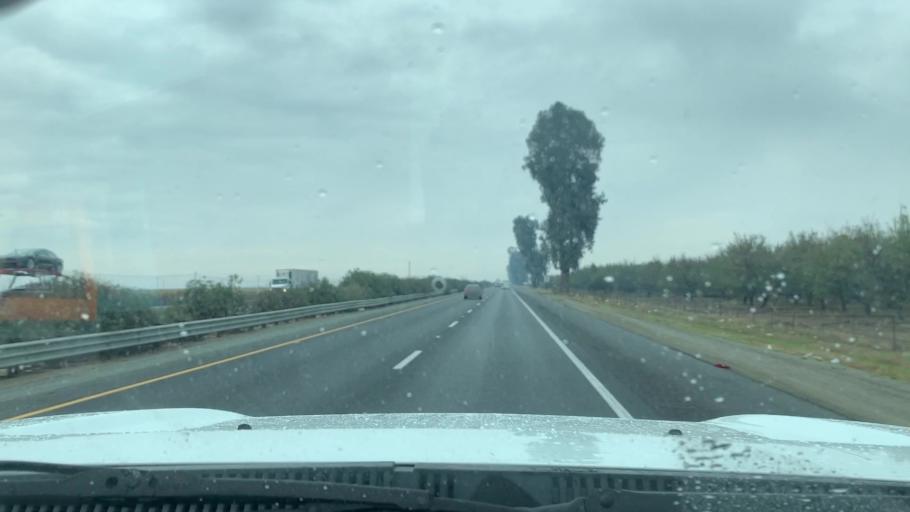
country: US
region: California
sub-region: Kern County
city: Delano
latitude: 35.8006
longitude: -119.2546
